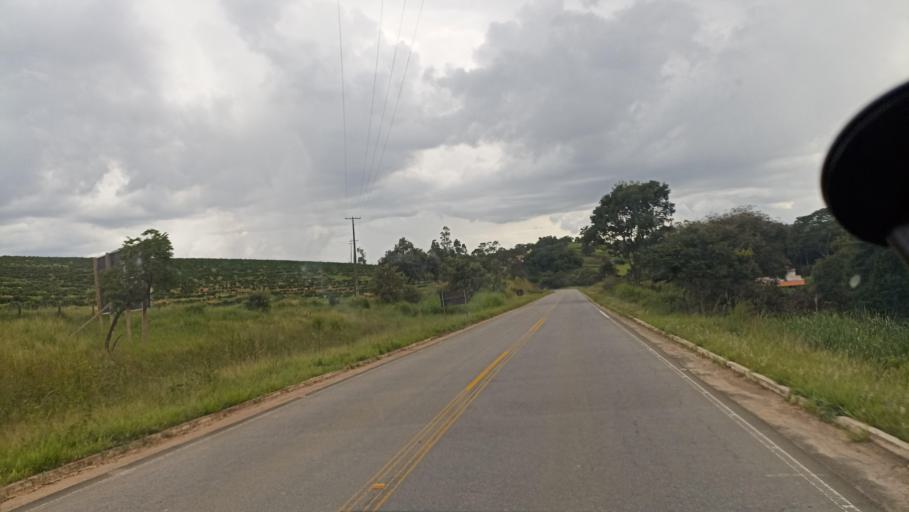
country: BR
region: Minas Gerais
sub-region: Cruzilia
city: Cruzilia
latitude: -21.8932
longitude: -44.8182
